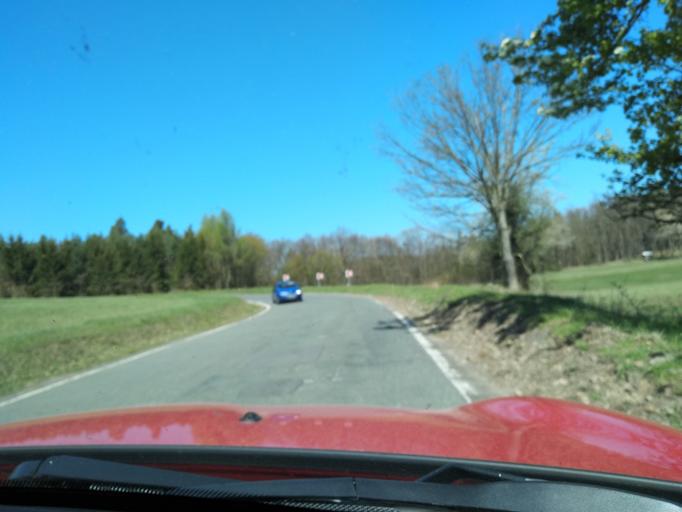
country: DE
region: Thuringia
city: Bad Blankenburg
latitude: 50.6521
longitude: 11.2820
